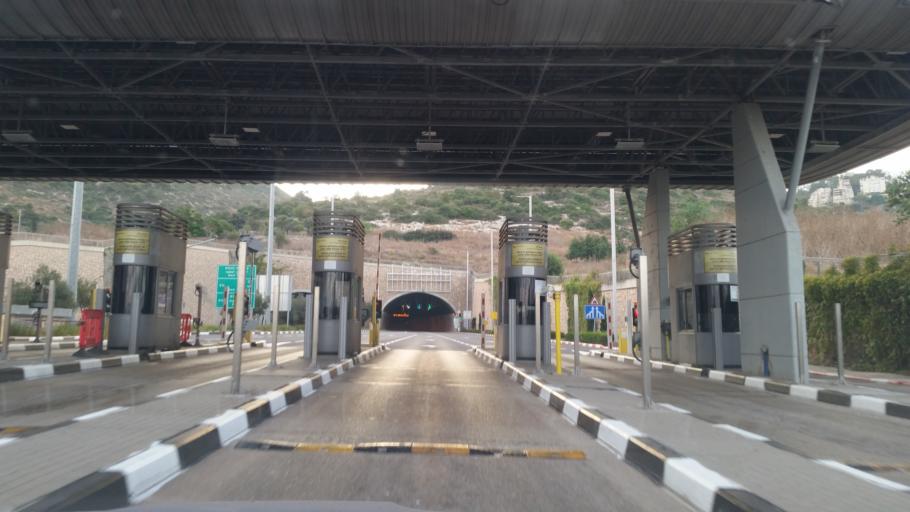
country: IL
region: Haifa
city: Tirat Karmel
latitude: 32.7922
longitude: 34.9692
